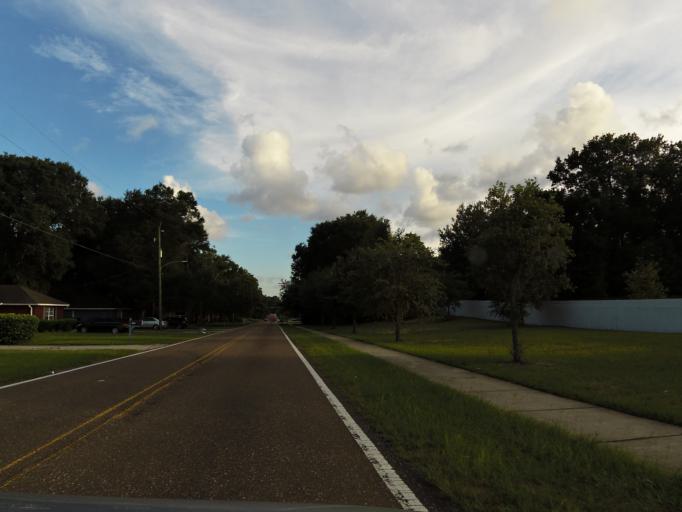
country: US
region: Florida
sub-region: Duval County
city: Jacksonville
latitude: 30.4079
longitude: -81.6974
